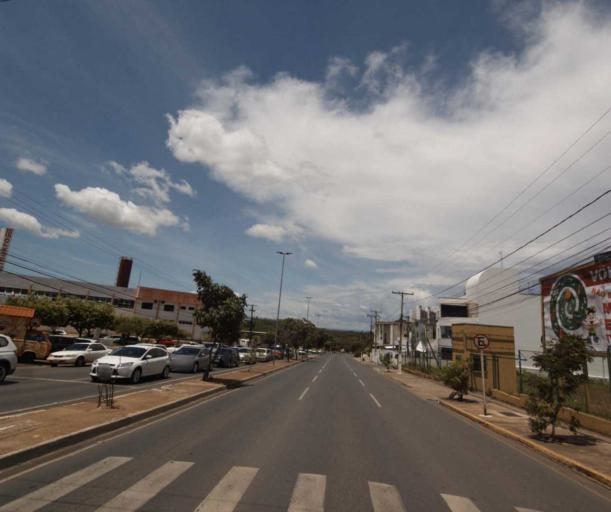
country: BR
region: Mato Grosso
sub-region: Cuiaba
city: Cuiaba
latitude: -15.5793
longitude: -56.1098
